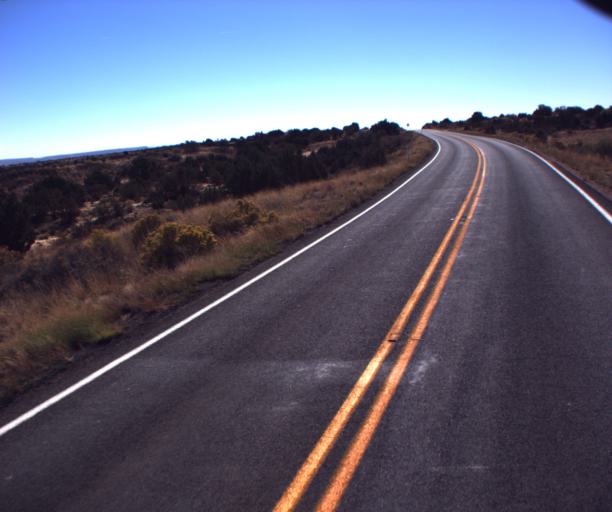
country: US
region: Arizona
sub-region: Navajo County
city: First Mesa
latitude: 35.9064
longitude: -110.6666
